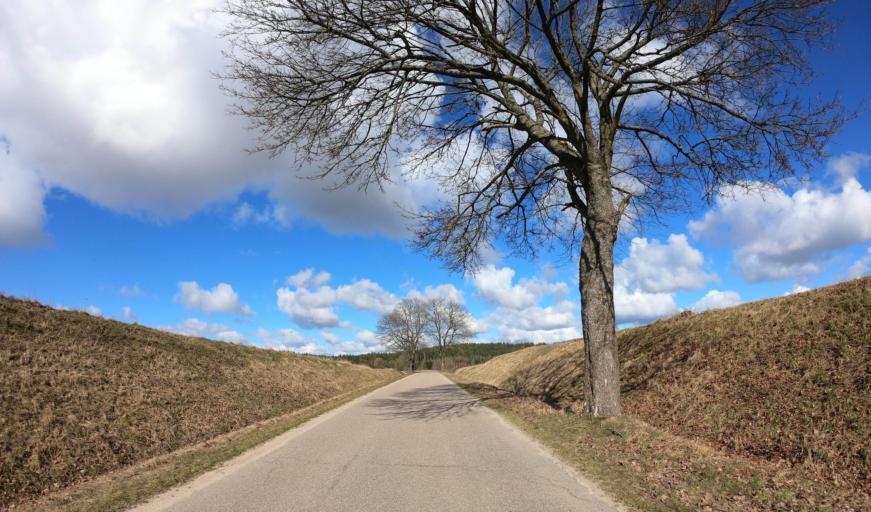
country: PL
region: West Pomeranian Voivodeship
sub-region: Powiat drawski
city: Zlocieniec
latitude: 53.4692
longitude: 15.9297
